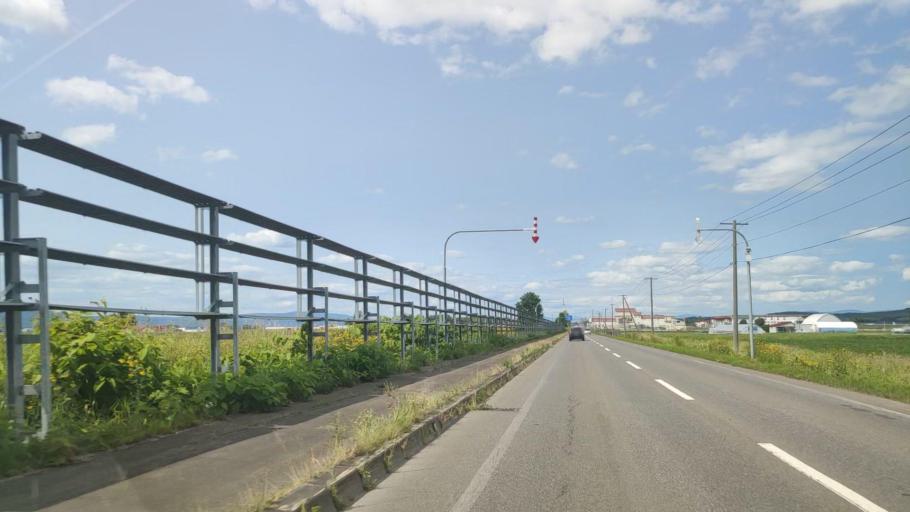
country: JP
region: Hokkaido
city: Nayoro
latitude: 44.1974
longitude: 142.4159
